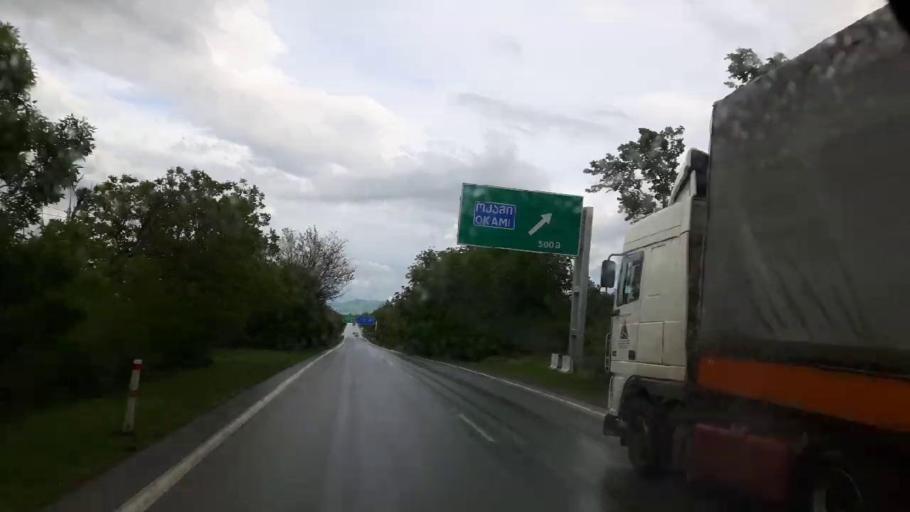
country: GE
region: Shida Kartli
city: Kaspi
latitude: 41.9665
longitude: 44.4640
